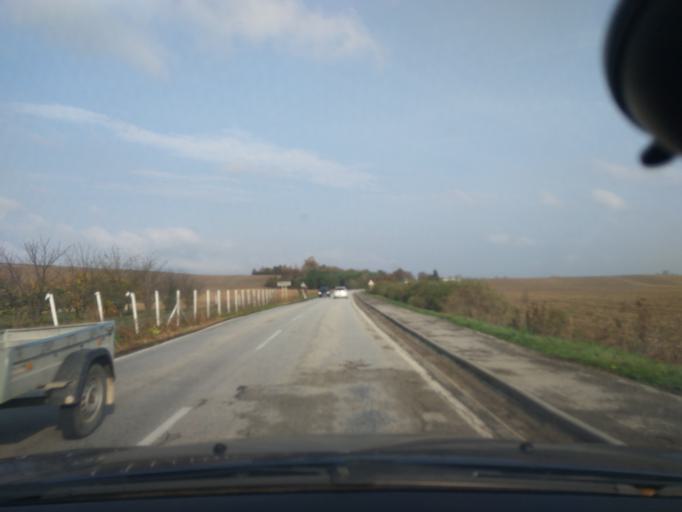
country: SK
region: Trnavsky
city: Vrbove
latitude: 48.6566
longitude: 17.7568
